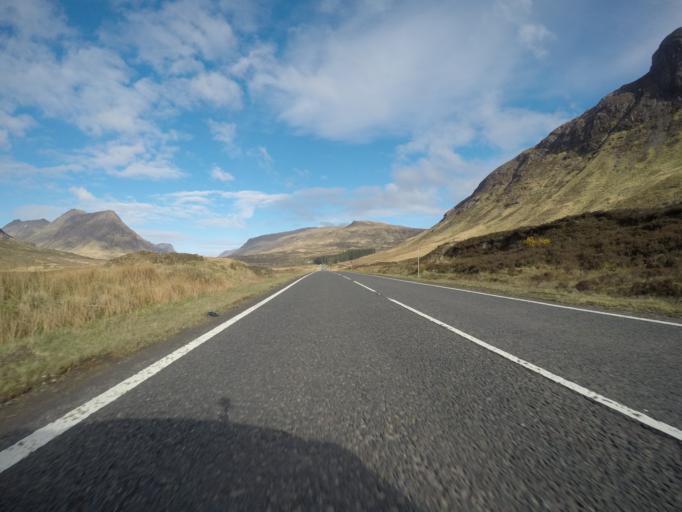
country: GB
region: Scotland
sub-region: Highland
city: Spean Bridge
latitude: 56.6612
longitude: -4.8909
